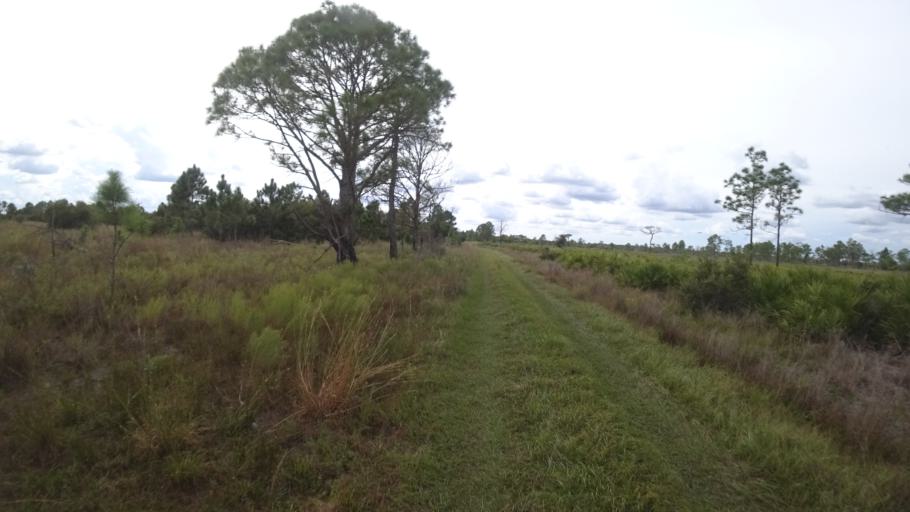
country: US
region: Florida
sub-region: Hillsborough County
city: Wimauma
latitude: 27.5536
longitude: -82.1381
